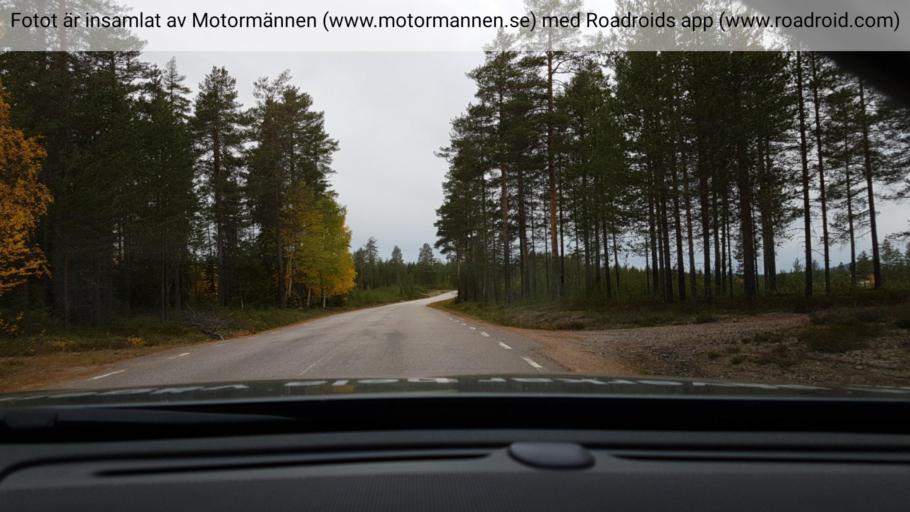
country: SE
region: Norrbotten
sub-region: Overkalix Kommun
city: OEverkalix
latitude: 66.2361
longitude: 22.9375
